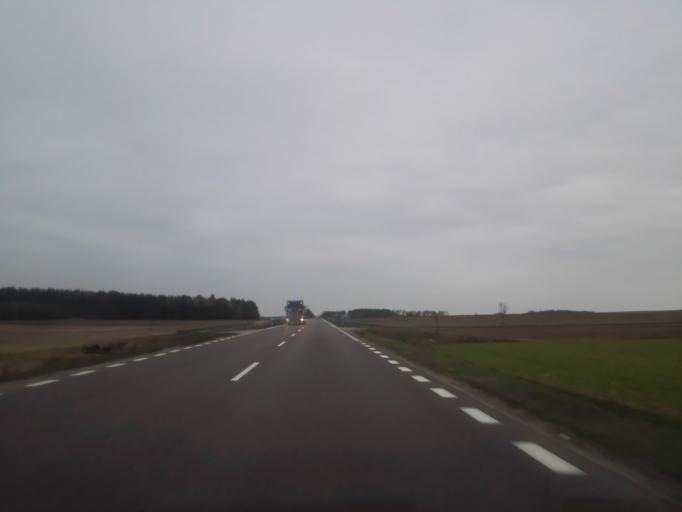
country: PL
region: Podlasie
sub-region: Powiat grajewski
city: Szczuczyn
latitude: 53.4801
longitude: 22.2138
